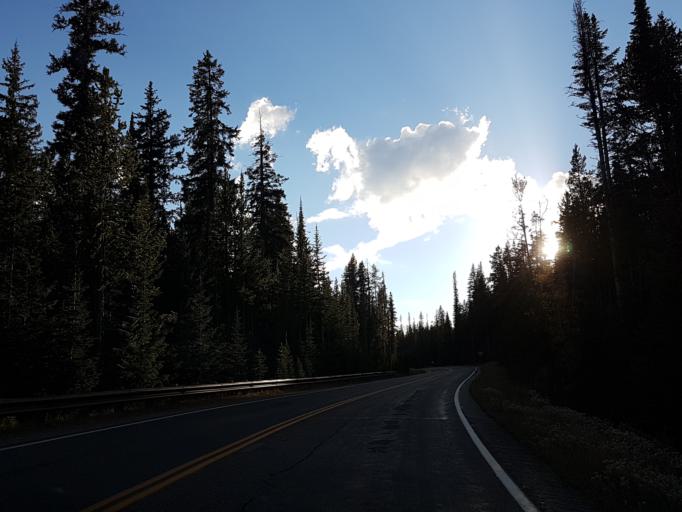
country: US
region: Montana
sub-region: Gallatin County
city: West Yellowstone
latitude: 44.4430
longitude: -110.7151
